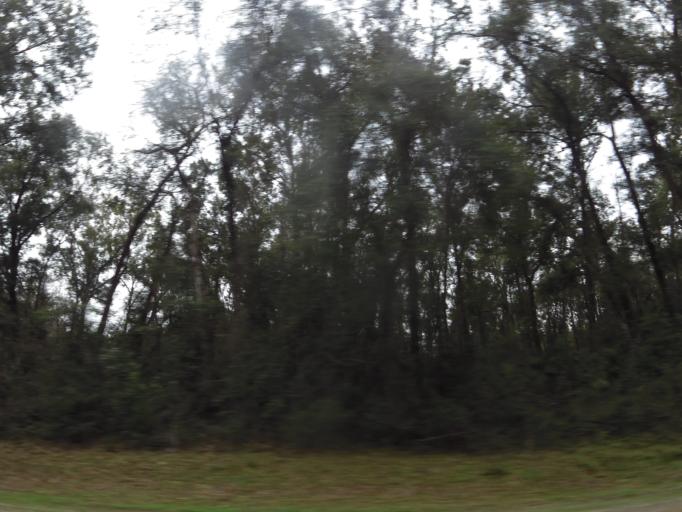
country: US
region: Florida
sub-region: Gilchrist County
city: Trenton
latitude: 29.7956
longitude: -82.9142
